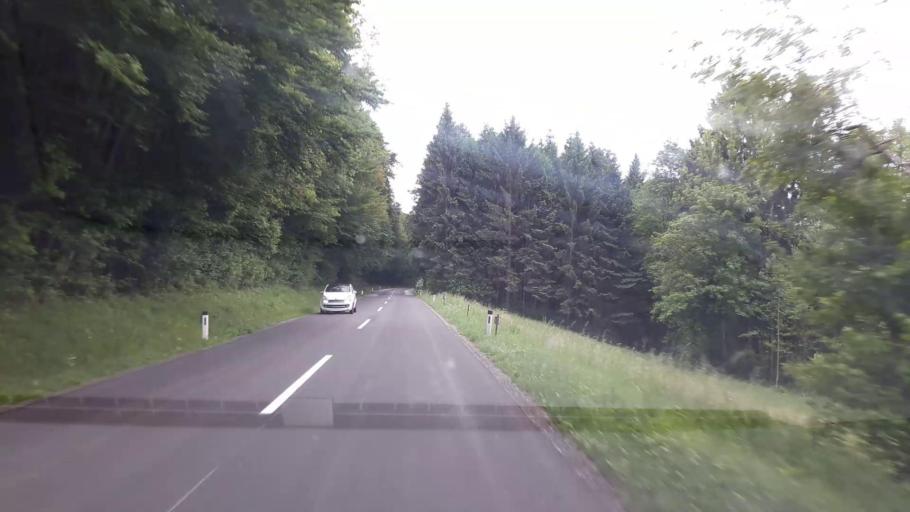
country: AT
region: Styria
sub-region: Politischer Bezirk Hartberg-Fuerstenfeld
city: Soechau
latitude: 47.0515
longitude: 16.0127
